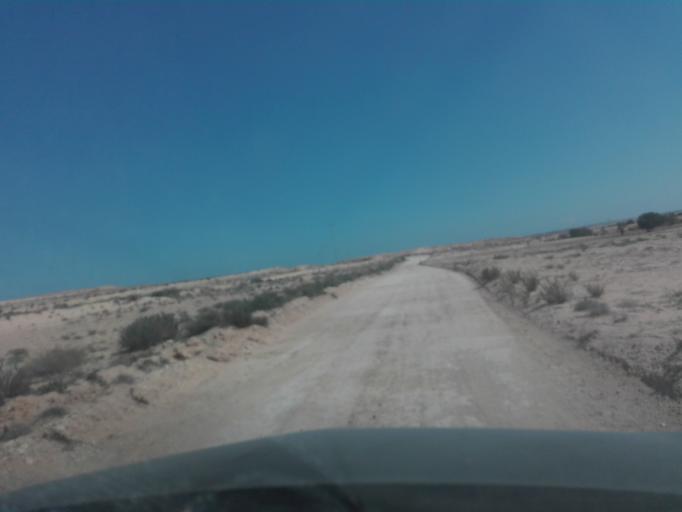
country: TN
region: Qabis
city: Gabes
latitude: 33.8445
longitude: 9.9870
